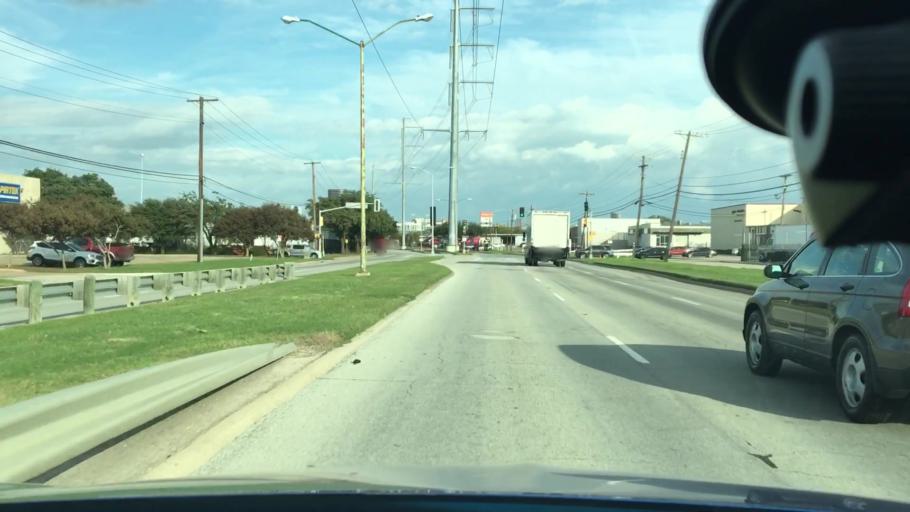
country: US
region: Texas
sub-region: Dallas County
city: Dallas
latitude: 32.8078
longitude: -96.8643
